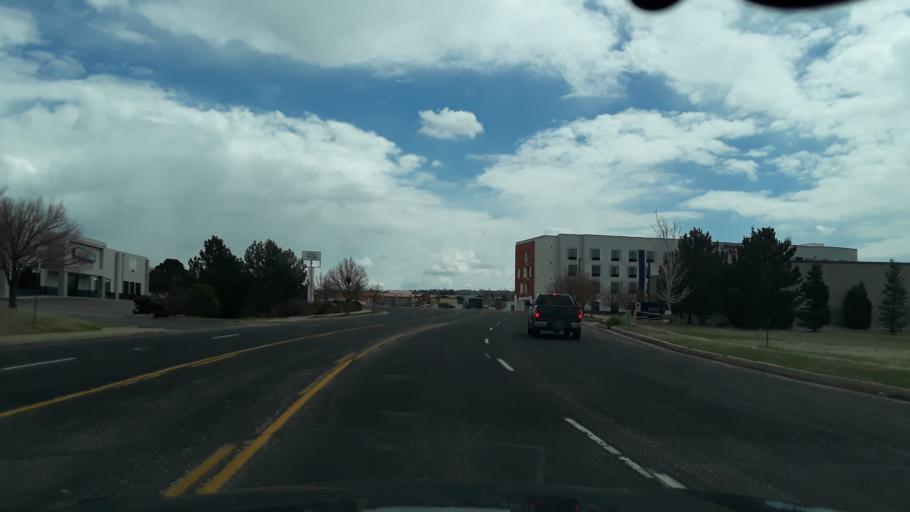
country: US
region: Colorado
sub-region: El Paso County
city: Air Force Academy
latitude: 38.9477
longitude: -104.8068
